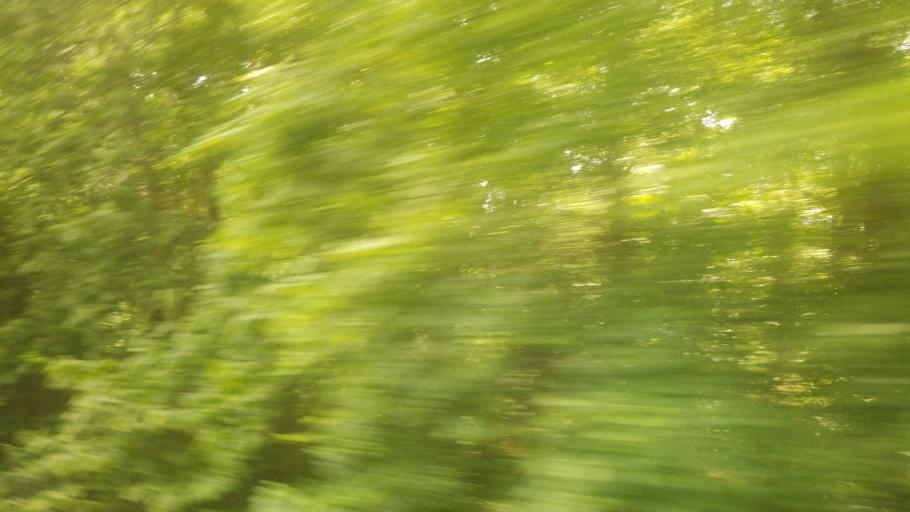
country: US
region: Maryland
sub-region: Frederick County
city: Point of Rocks
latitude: 39.2555
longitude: -77.4917
